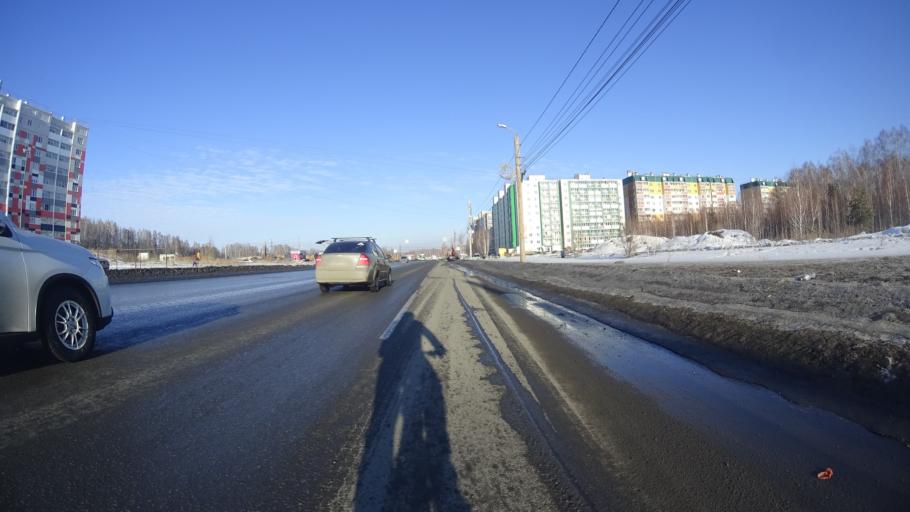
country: RU
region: Chelyabinsk
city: Roshchino
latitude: 55.2174
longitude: 61.2899
